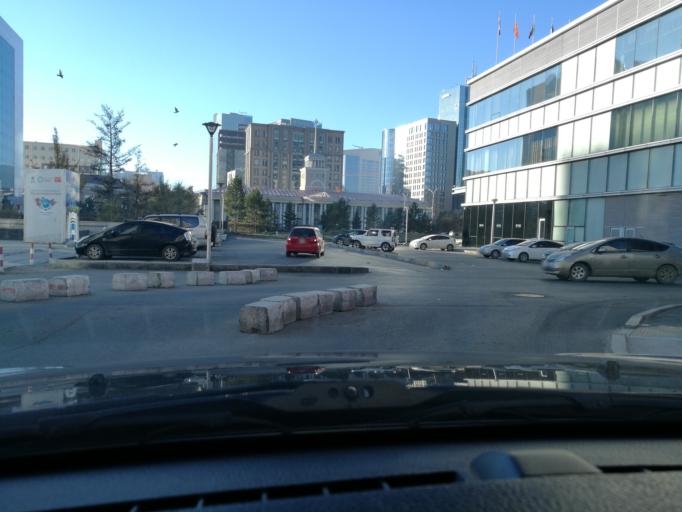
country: MN
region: Ulaanbaatar
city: Ulaanbaatar
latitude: 47.9188
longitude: 106.9212
